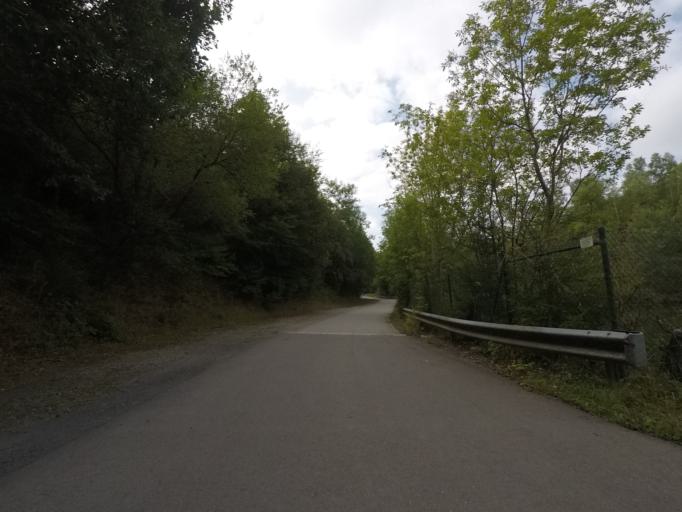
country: BE
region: Wallonia
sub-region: Province du Luxembourg
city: Martelange
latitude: 49.8246
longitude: 5.7543
